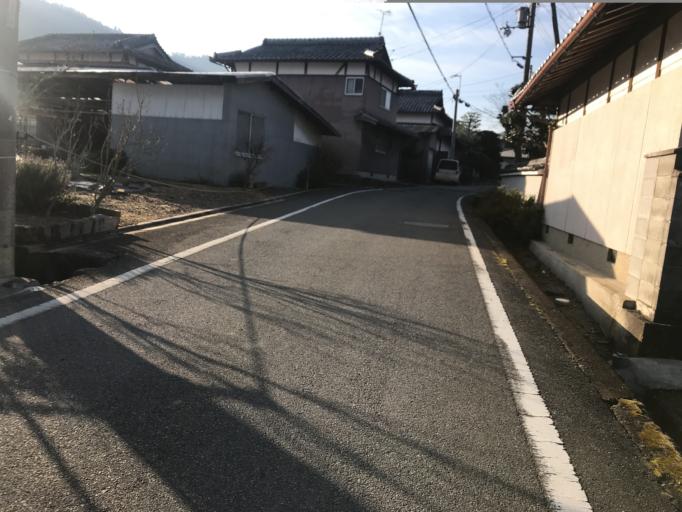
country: JP
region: Kyoto
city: Kameoka
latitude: 34.9904
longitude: 135.5495
